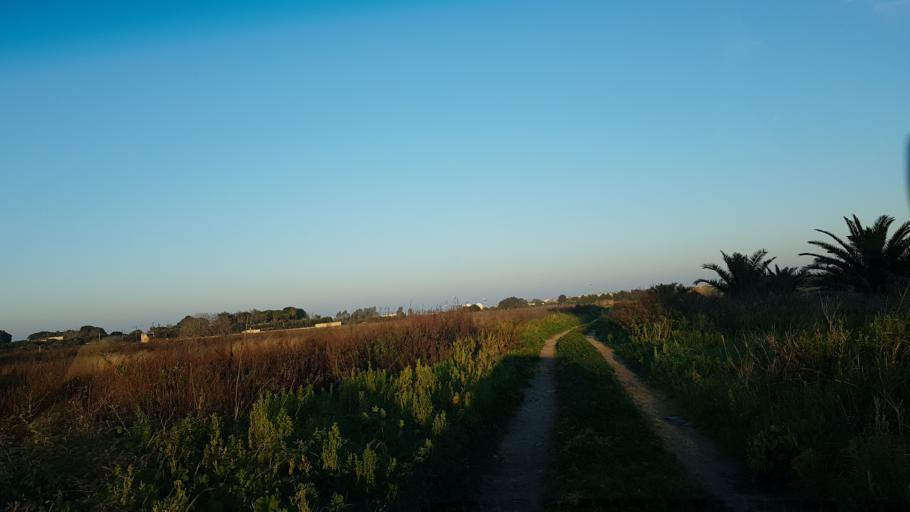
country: IT
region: Apulia
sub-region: Provincia di Brindisi
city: Brindisi
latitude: 40.6512
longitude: 17.9234
